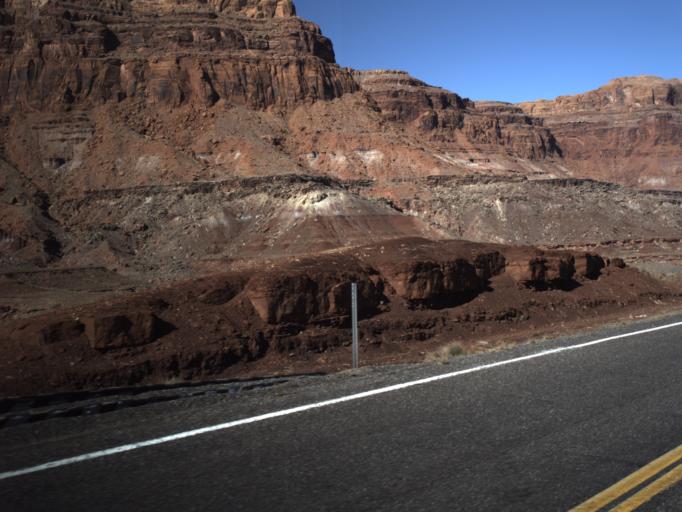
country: US
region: Utah
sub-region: San Juan County
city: Blanding
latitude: 37.8841
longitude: -110.4265
